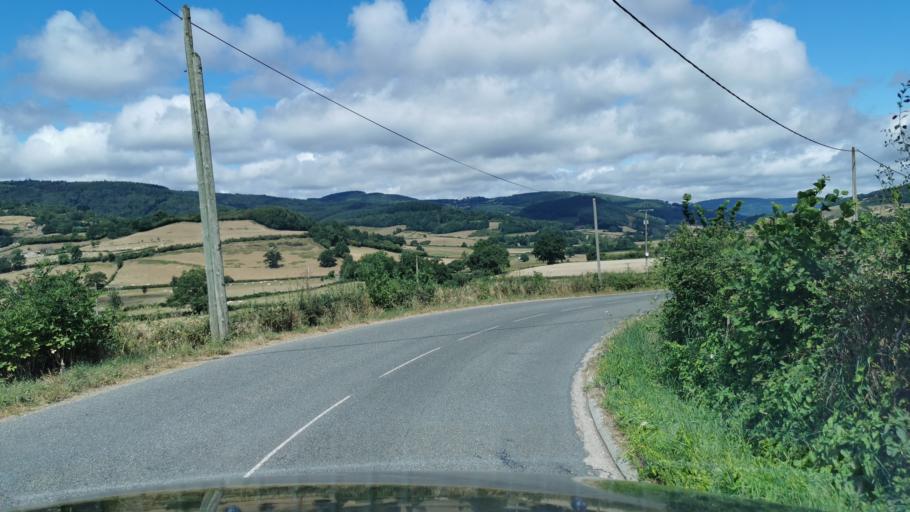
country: FR
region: Bourgogne
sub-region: Departement de Saone-et-Loire
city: Marmagne
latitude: 46.8052
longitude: 4.3358
